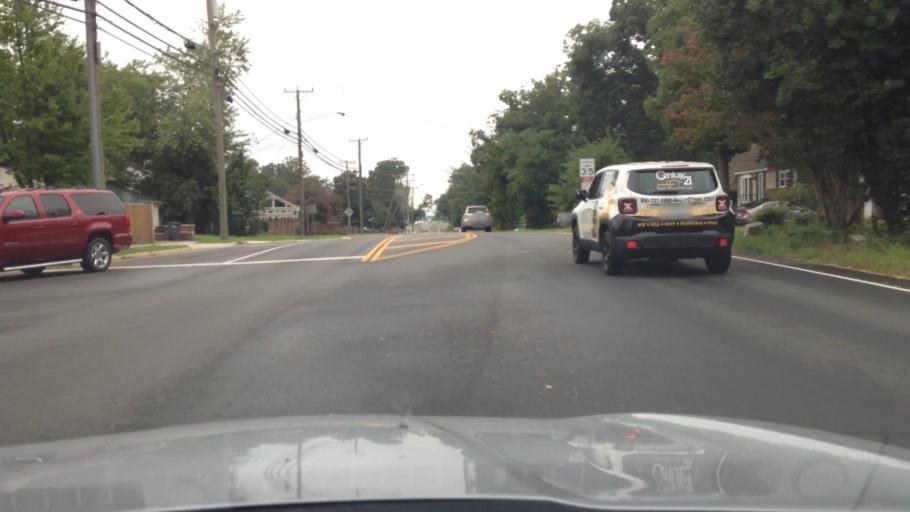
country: US
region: Virginia
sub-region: Fairfax County
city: Groveton
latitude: 38.7735
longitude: -77.0937
